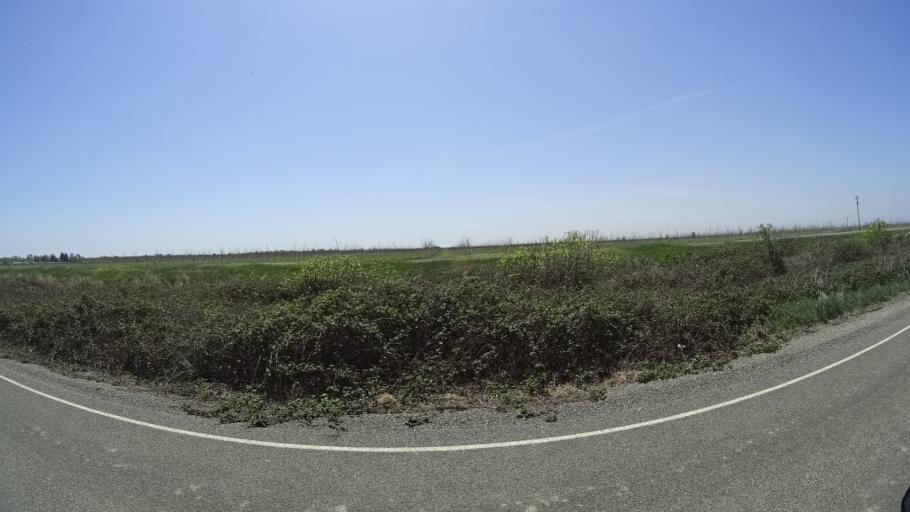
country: US
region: California
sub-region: Glenn County
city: Willows
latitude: 39.5581
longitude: -122.0127
